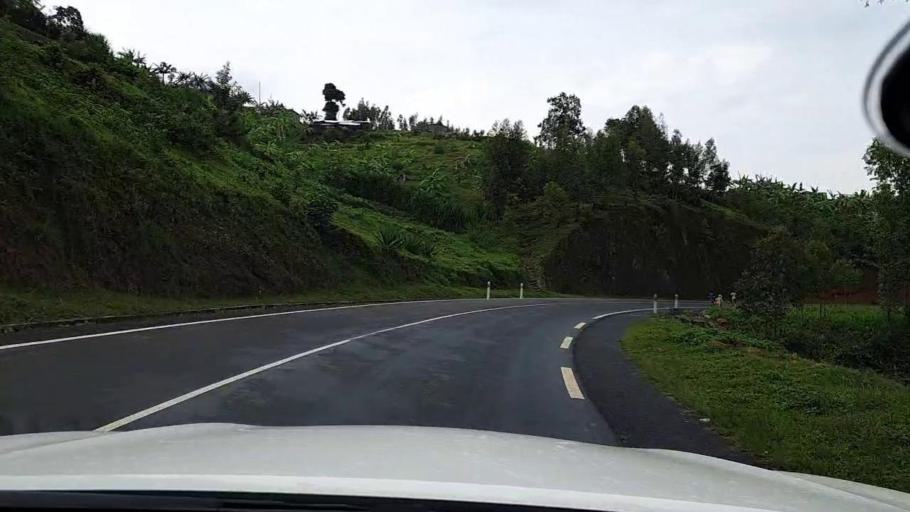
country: RW
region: Western Province
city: Kibuye
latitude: -2.1575
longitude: 29.2969
